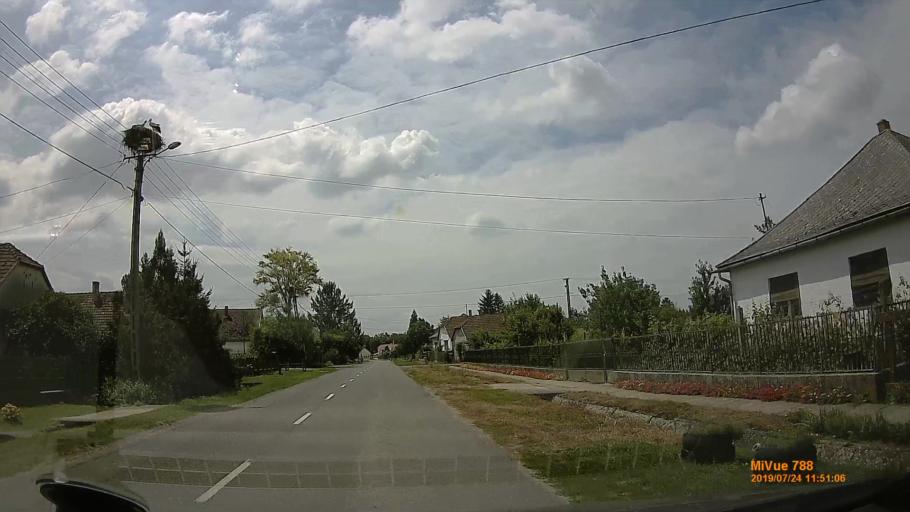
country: UA
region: Zakarpattia
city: Batiovo
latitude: 48.2363
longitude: 22.4342
